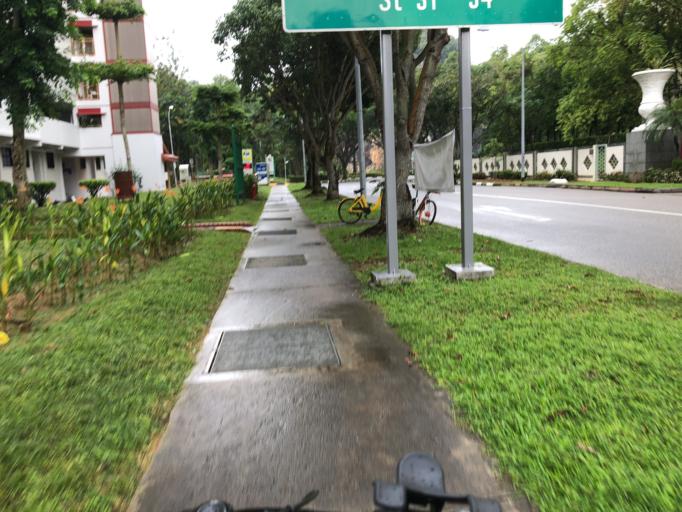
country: MY
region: Johor
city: Johor Bahru
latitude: 1.3565
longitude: 103.7523
